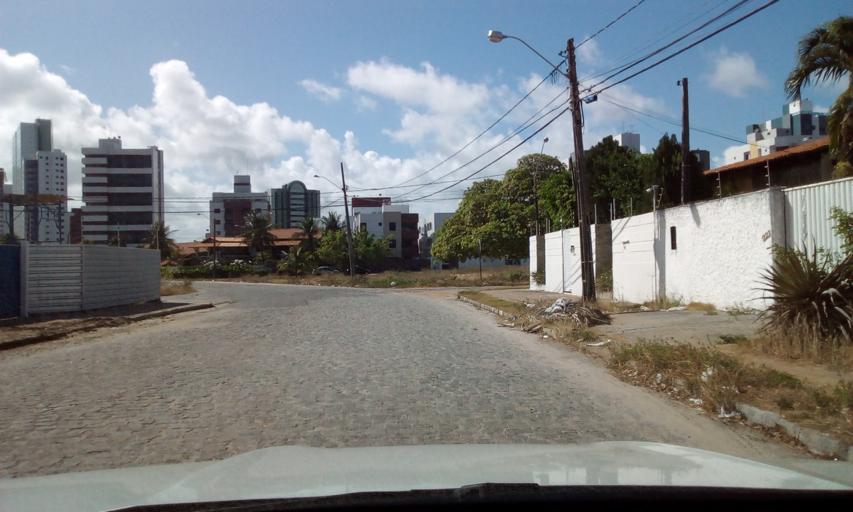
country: BR
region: Paraiba
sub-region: Joao Pessoa
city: Joao Pessoa
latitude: -7.0817
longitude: -34.8334
